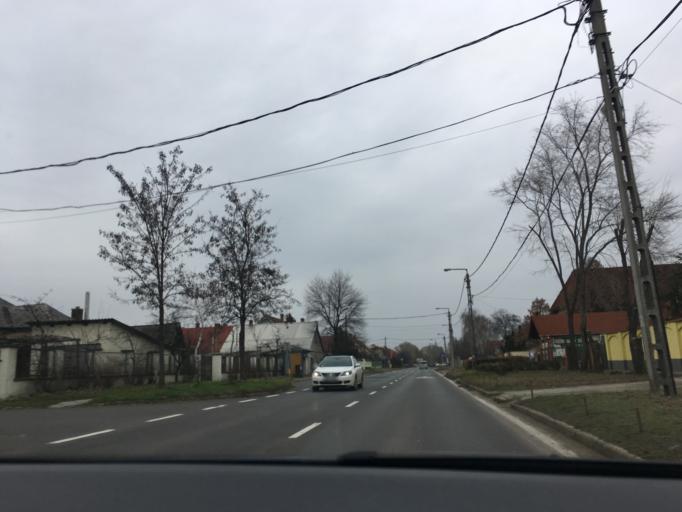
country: HU
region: Hajdu-Bihar
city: Debrecen
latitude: 47.5339
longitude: 21.6713
